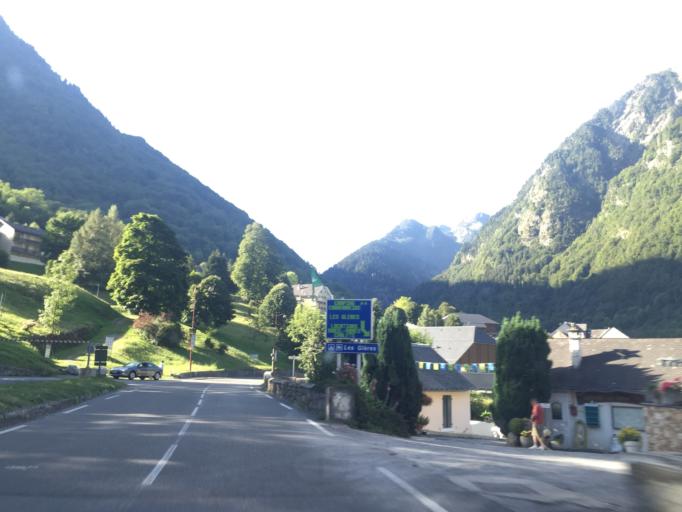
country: FR
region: Midi-Pyrenees
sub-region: Departement des Hautes-Pyrenees
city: Cauterets
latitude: 42.8944
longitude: -0.1126
